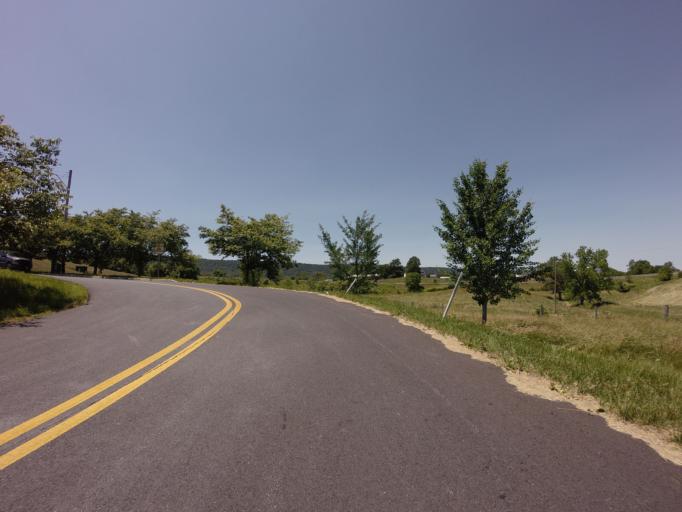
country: US
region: Maryland
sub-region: Frederick County
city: Brunswick
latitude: 39.3409
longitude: -77.6352
